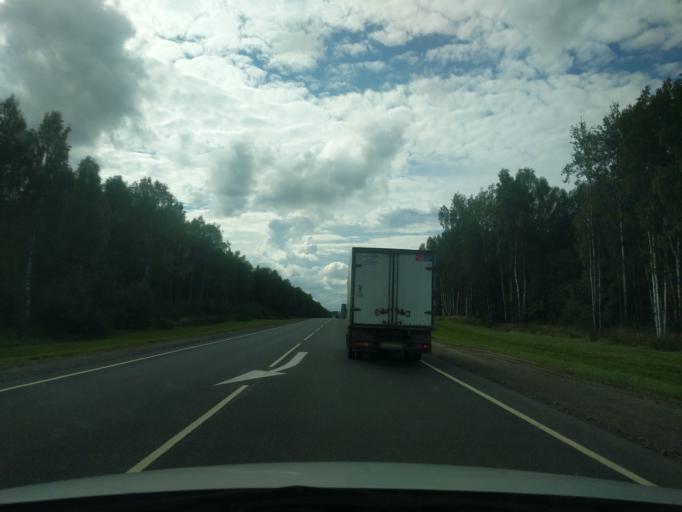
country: RU
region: Jaroslavl
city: Levashevo
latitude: 57.6381
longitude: 40.4508
